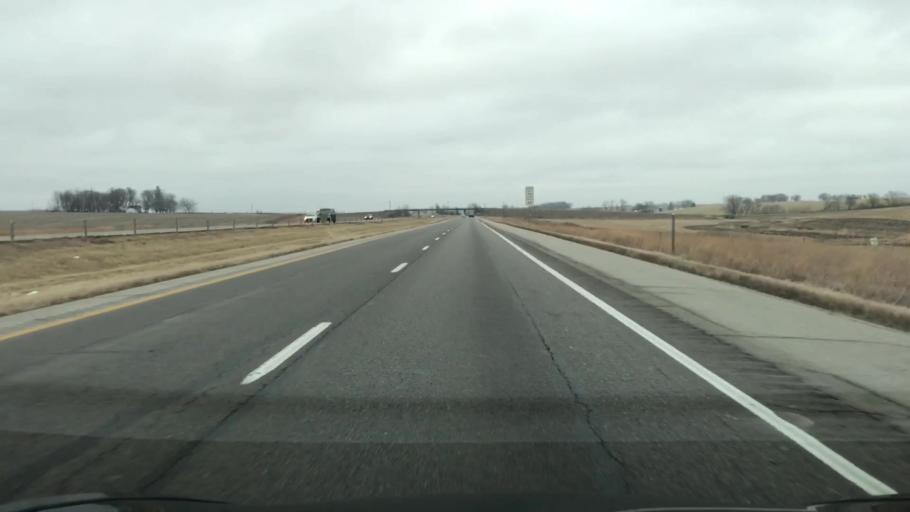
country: US
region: Iowa
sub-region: Guthrie County
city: Stuart
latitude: 41.4934
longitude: -94.2321
